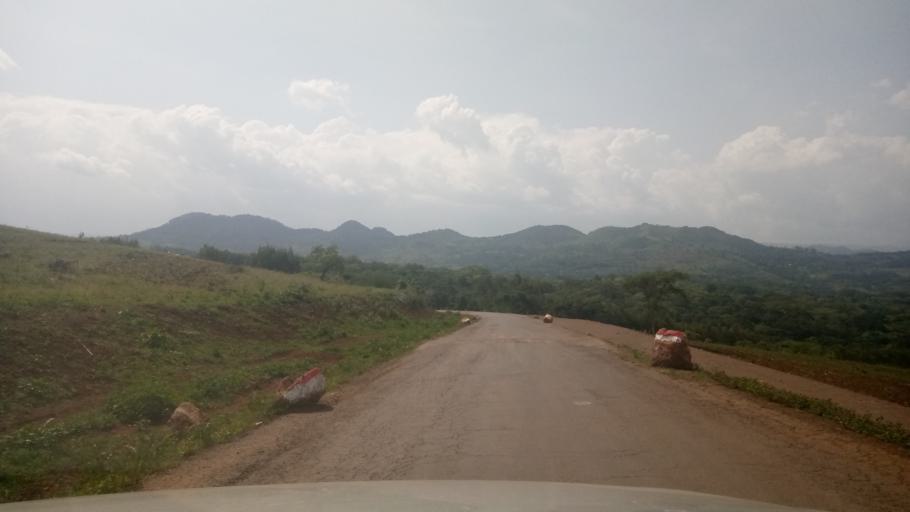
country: ET
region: Oromiya
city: Agaro
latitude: 7.9891
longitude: 36.5109
